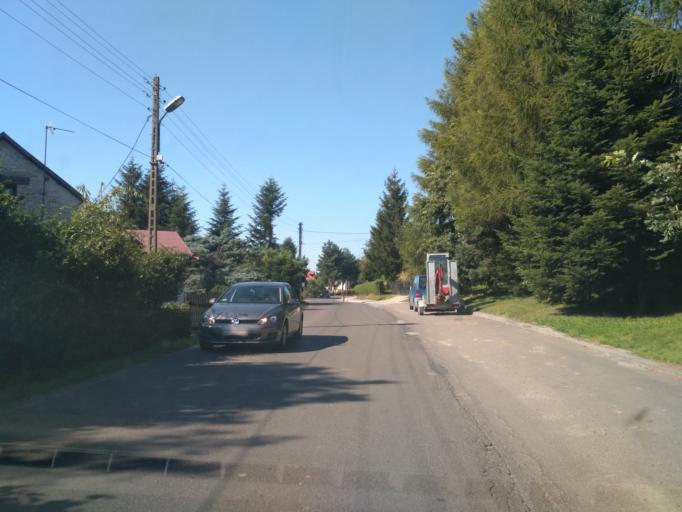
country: PL
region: Subcarpathian Voivodeship
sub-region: Krosno
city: Krosno
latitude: 49.6628
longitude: 21.7524
